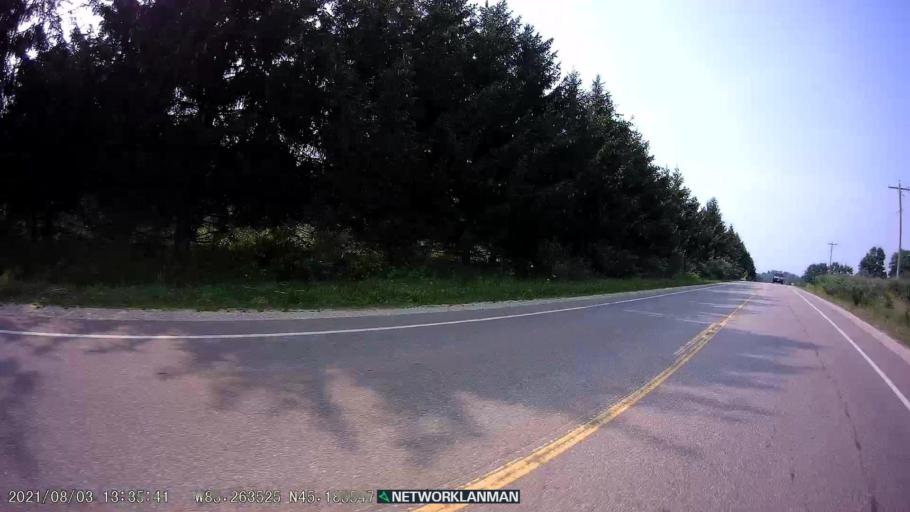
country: US
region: Michigan
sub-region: Charlevoix County
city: Charlevoix
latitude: 45.1857
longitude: -85.2632
